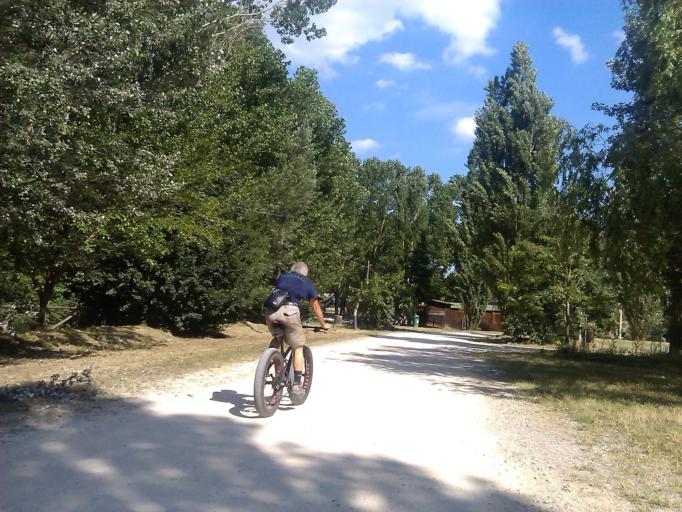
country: IT
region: Tuscany
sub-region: Provincia di Siena
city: Chiusi
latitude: 43.0496
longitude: 11.9595
